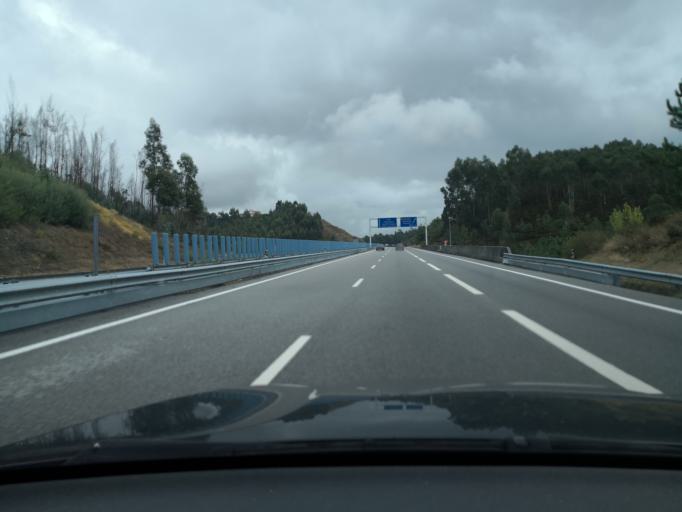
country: PT
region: Porto
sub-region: Lousada
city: Lousada
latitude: 41.2943
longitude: -8.2952
